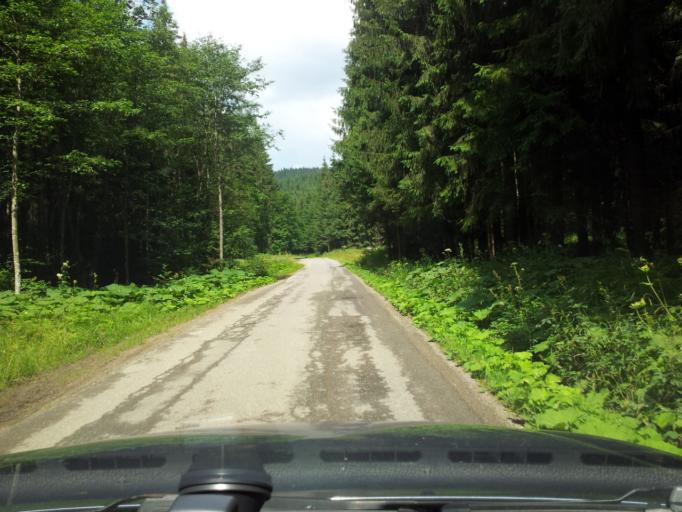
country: SK
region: Zilinsky
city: Oravska Lesna
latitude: 49.3859
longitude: 19.2160
